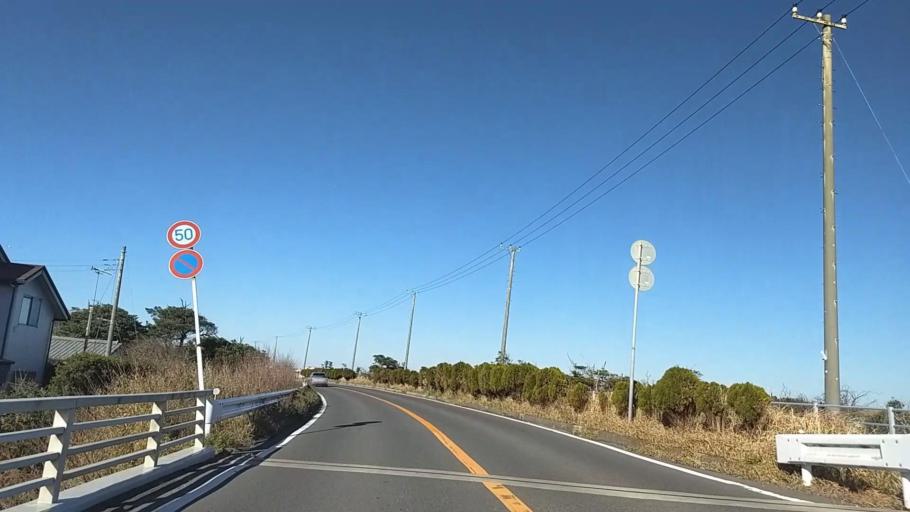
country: JP
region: Chiba
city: Ohara
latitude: 35.3480
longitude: 140.3910
